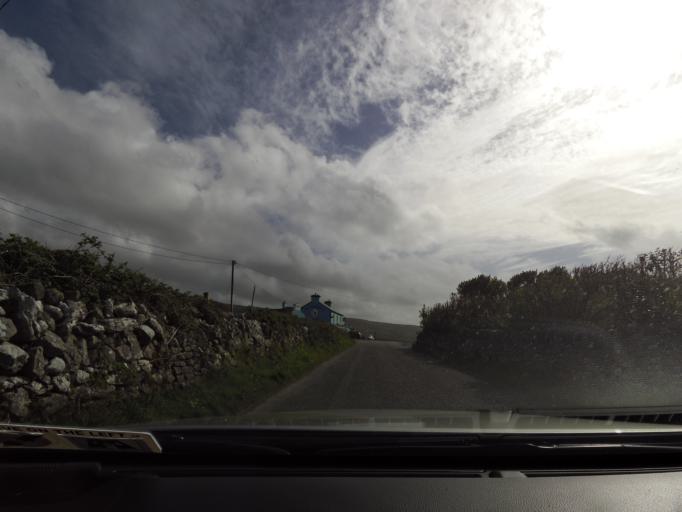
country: IE
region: Connaught
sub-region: County Galway
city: Bearna
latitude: 53.1024
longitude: -9.2966
